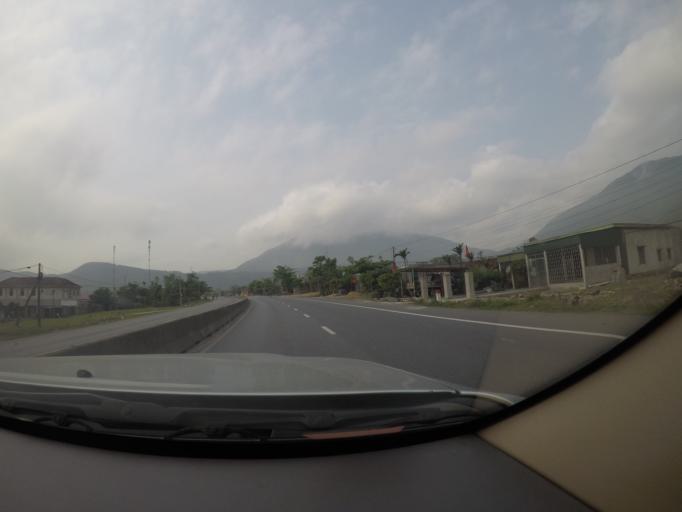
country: VN
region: Ha Tinh
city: Ky Anh
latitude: 17.9721
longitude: 106.4713
